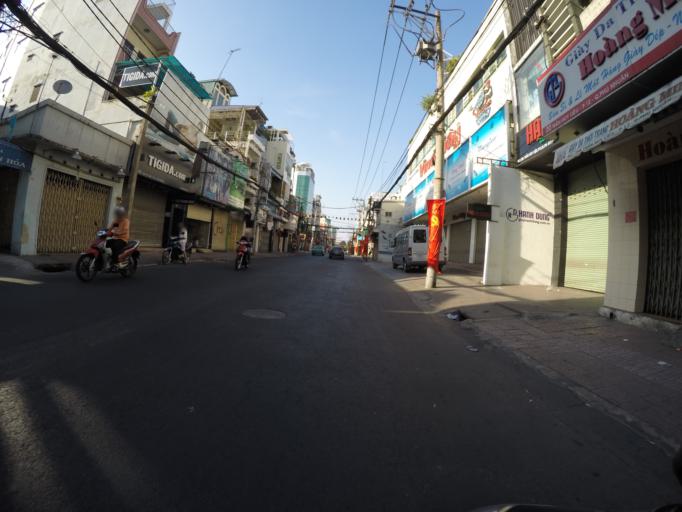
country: VN
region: Ho Chi Minh City
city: Quan Phu Nhuan
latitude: 10.7915
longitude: 106.6780
